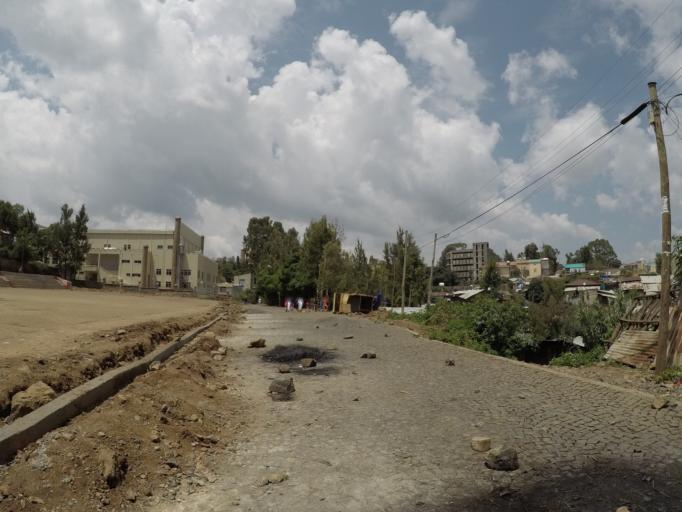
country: ET
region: Amhara
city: Gondar
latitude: 12.6127
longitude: 37.4725
